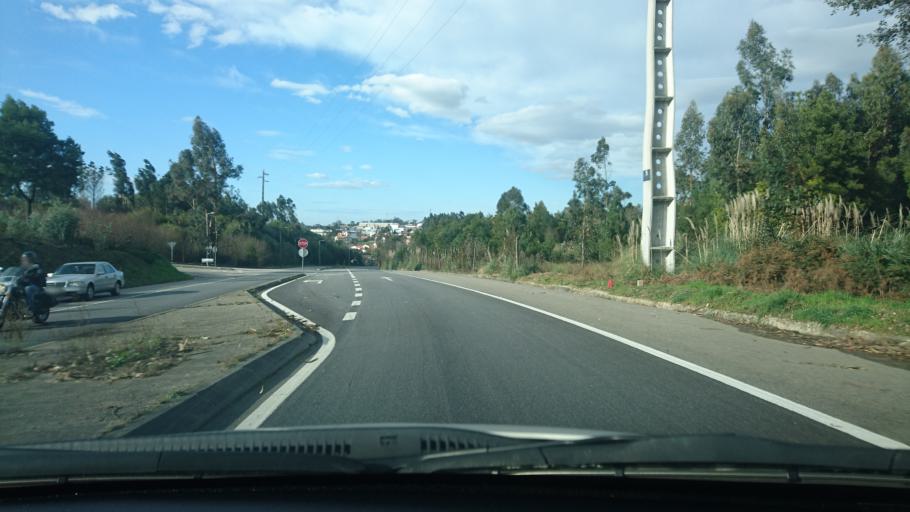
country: PT
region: Aveiro
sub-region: Santa Maria da Feira
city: Rio Meao
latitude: 40.9623
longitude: -8.5904
